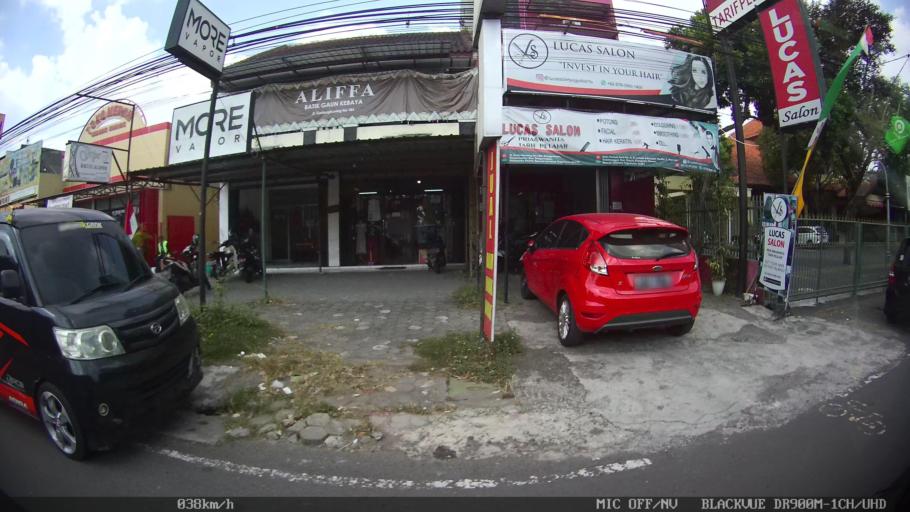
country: ID
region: Daerah Istimewa Yogyakarta
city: Yogyakarta
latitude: -7.8089
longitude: 110.4022
